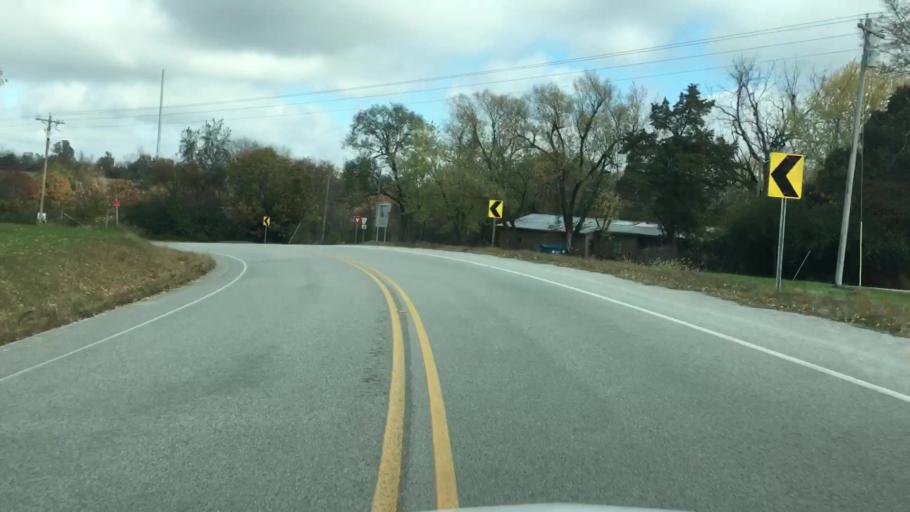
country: US
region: Arkansas
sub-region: Benton County
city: Centerton
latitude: 36.2619
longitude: -94.3509
